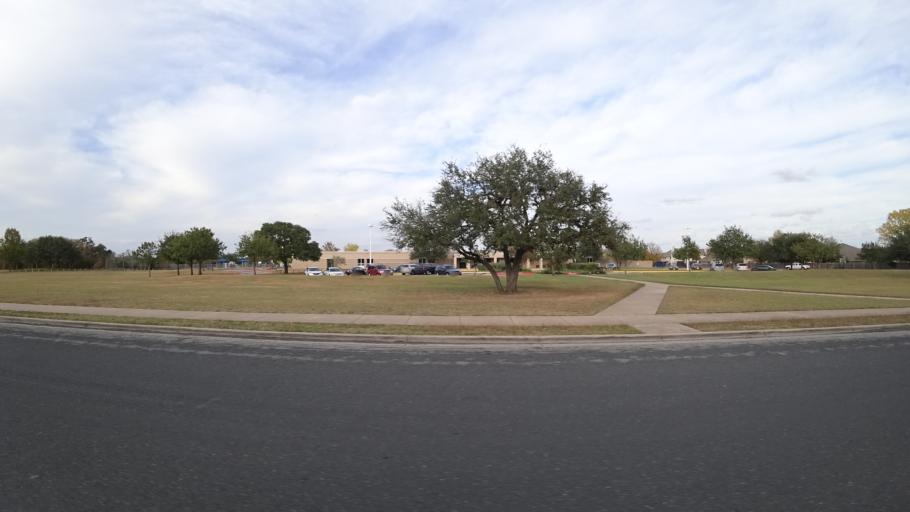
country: US
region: Texas
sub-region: Williamson County
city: Brushy Creek
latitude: 30.5155
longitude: -97.7207
